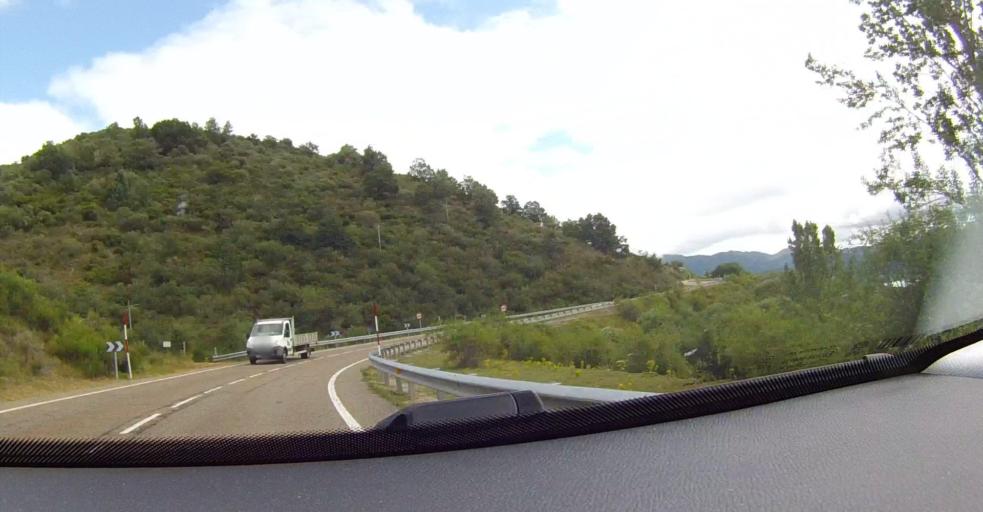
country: ES
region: Castille and Leon
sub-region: Provincia de Leon
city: Riano
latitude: 42.9947
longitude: -4.9939
